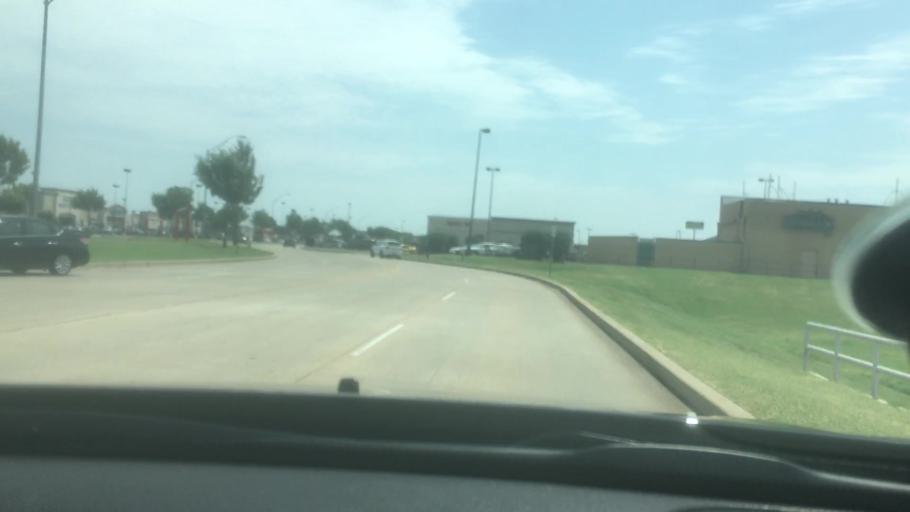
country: US
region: Oklahoma
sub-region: Oklahoma County
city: Bethany
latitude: 35.4616
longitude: -97.6294
